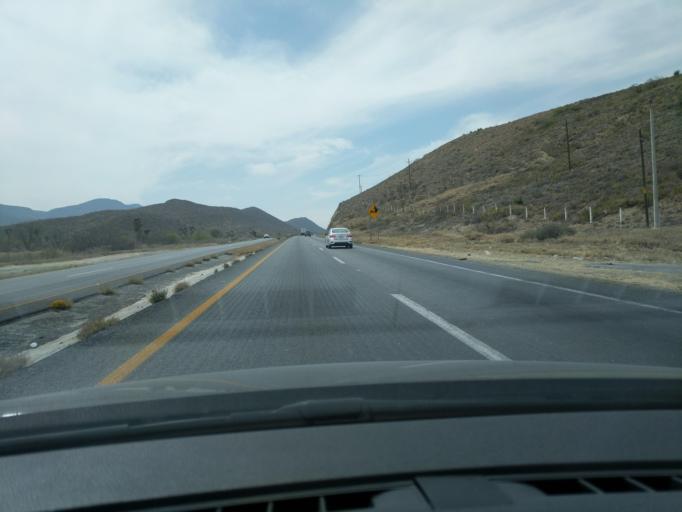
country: MX
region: Coahuila
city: Saltillo
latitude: 25.4531
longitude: -101.0827
